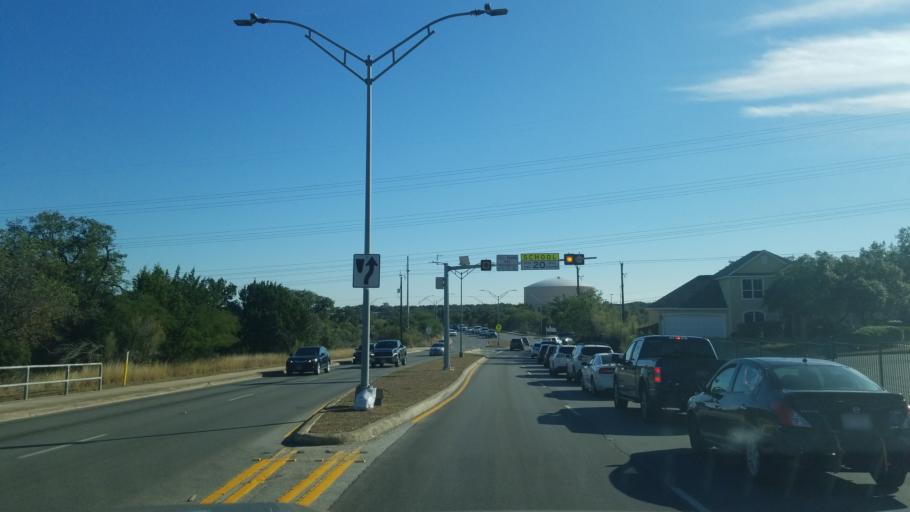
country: US
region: Texas
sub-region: Bexar County
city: Hollywood Park
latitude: 29.6326
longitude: -98.4814
